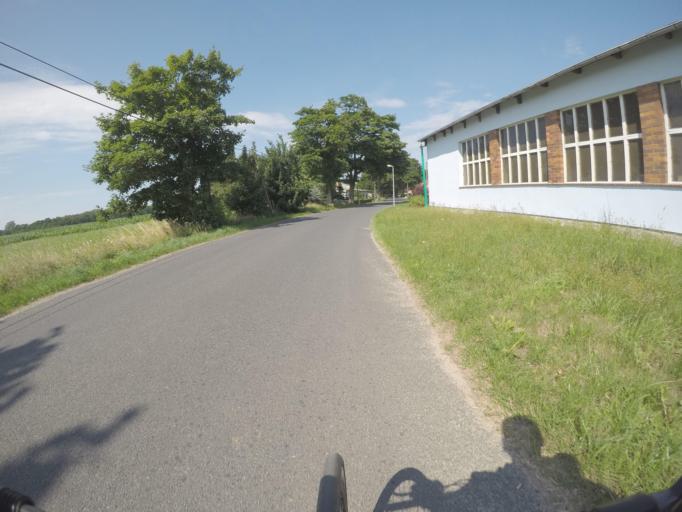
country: DE
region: Mecklenburg-Vorpommern
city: Gingst
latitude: 54.4376
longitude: 13.2222
